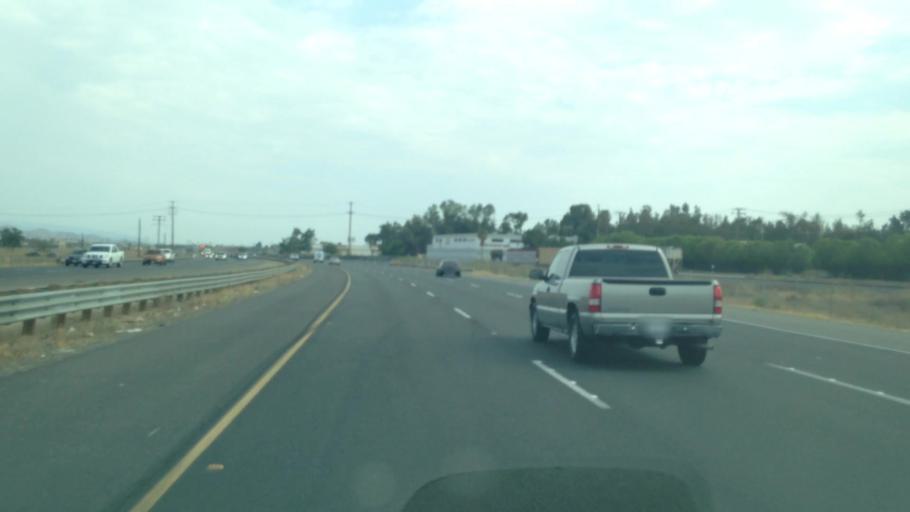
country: US
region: California
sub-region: Riverside County
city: Perris
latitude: 33.8184
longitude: -117.2402
